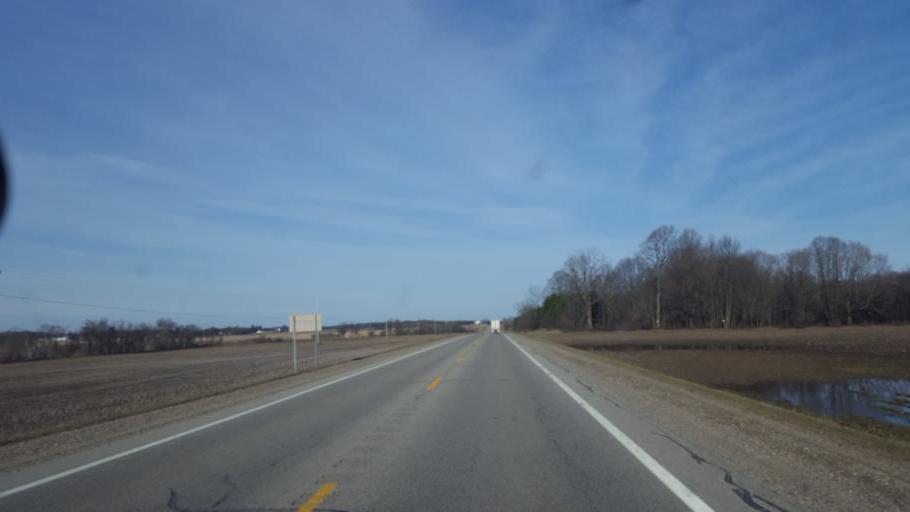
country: US
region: Michigan
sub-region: Montcalm County
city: Lakeview
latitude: 43.4301
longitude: -85.1864
